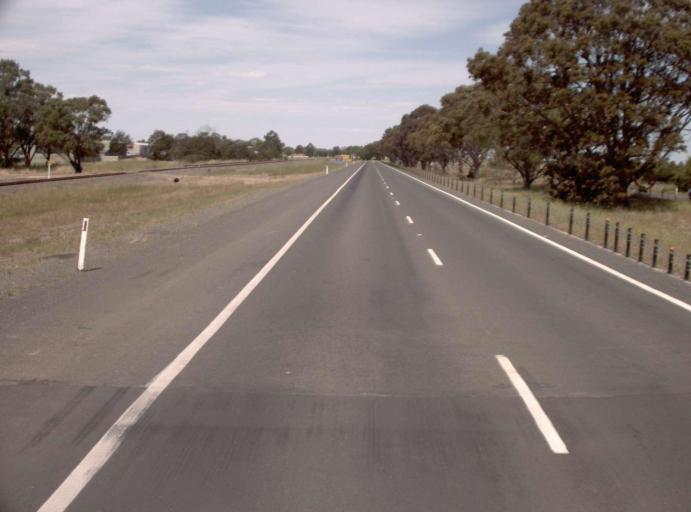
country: AU
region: Victoria
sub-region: Wellington
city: Sale
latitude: -38.1034
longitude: 147.0223
